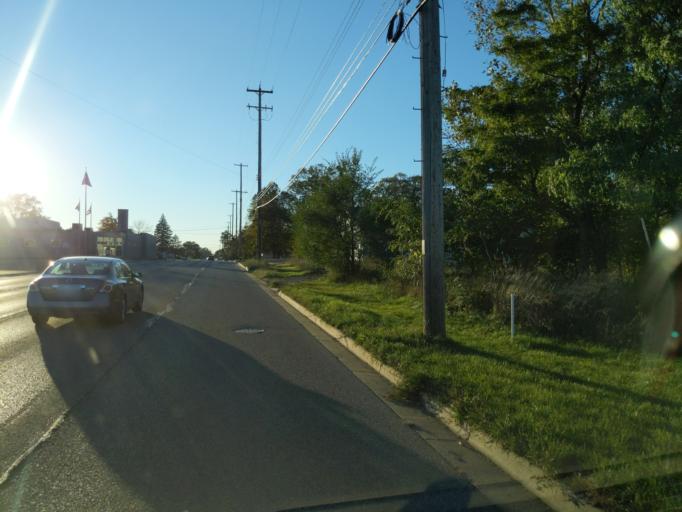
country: US
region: Michigan
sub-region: Ingham County
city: Edgemont Park
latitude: 42.7266
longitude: -84.5955
